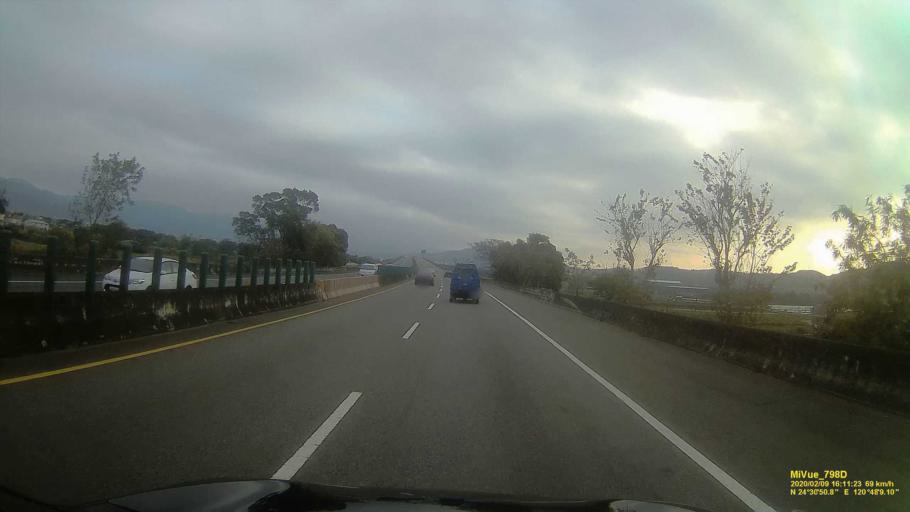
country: TW
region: Taiwan
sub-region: Miaoli
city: Miaoli
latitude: 24.5138
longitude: 120.8025
